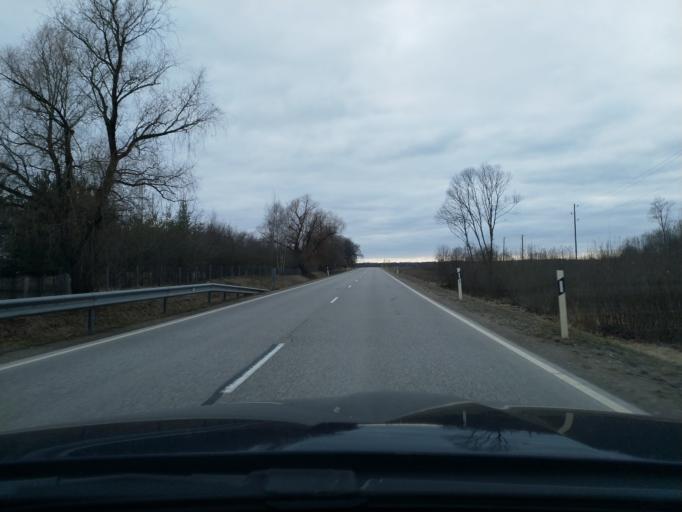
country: LV
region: Kuldigas Rajons
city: Kuldiga
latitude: 56.9626
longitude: 22.0713
